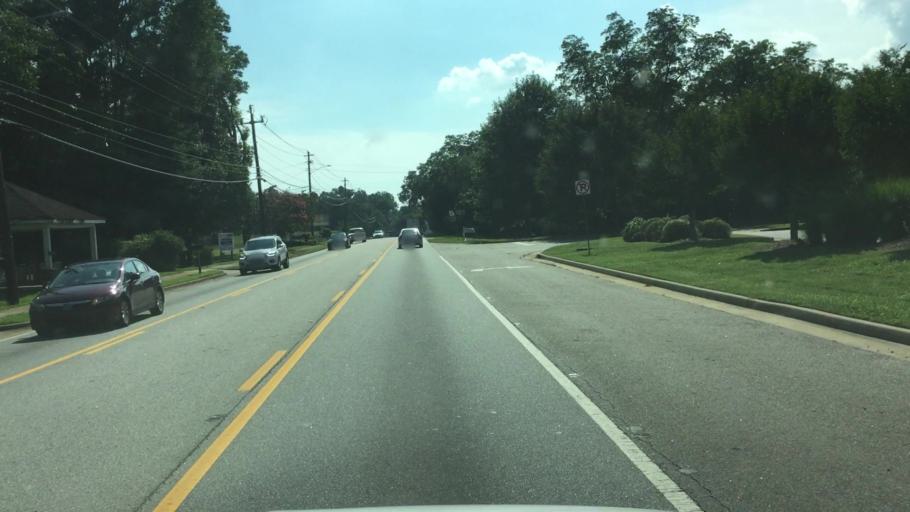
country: US
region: Georgia
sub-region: Barrow County
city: Auburn
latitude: 34.0126
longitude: -83.8301
